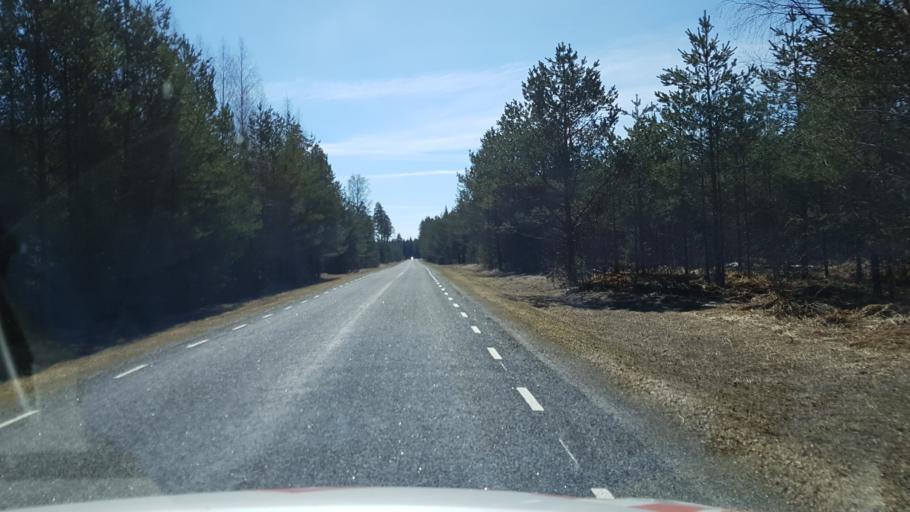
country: EE
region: Laeaene-Virumaa
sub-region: Vinni vald
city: Vinni
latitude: 59.1368
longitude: 26.5249
